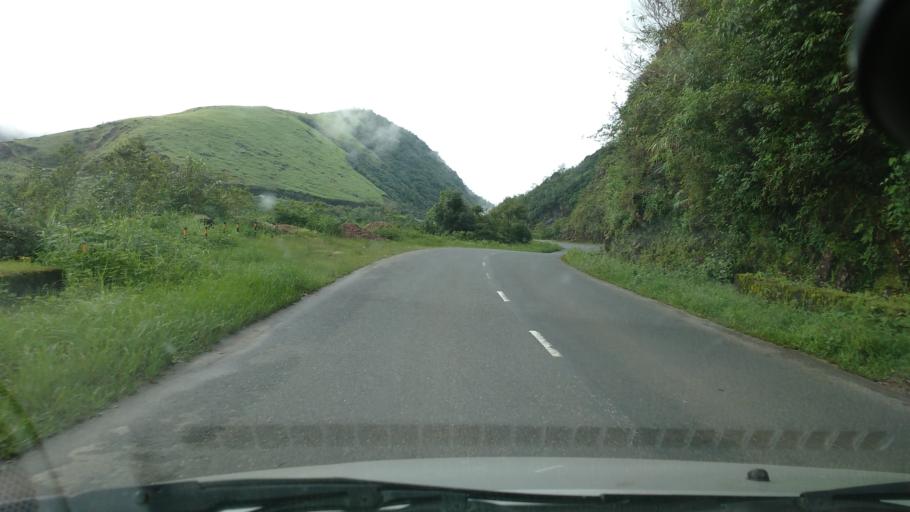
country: IN
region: Meghalaya
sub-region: East Khasi Hills
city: Shillong
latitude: 25.3840
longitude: 91.8743
